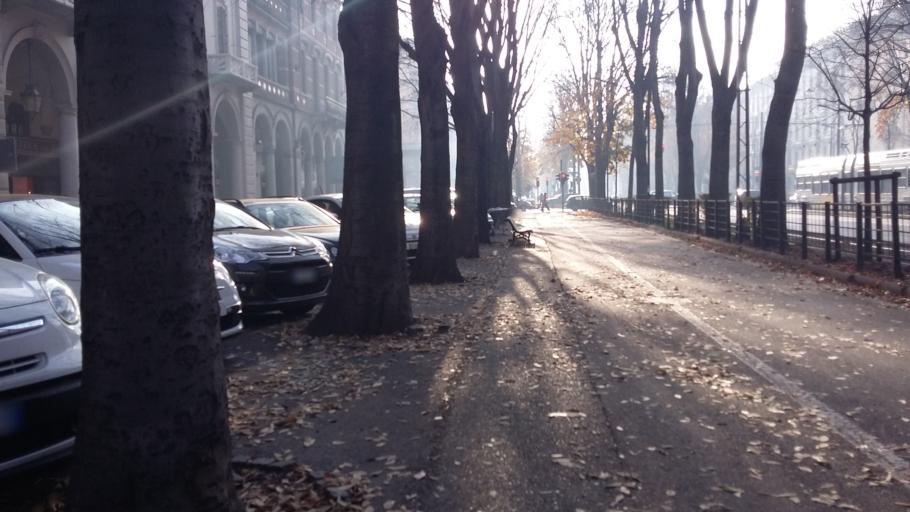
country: IT
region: Piedmont
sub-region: Provincia di Torino
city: Turin
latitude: 45.0697
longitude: 7.6681
